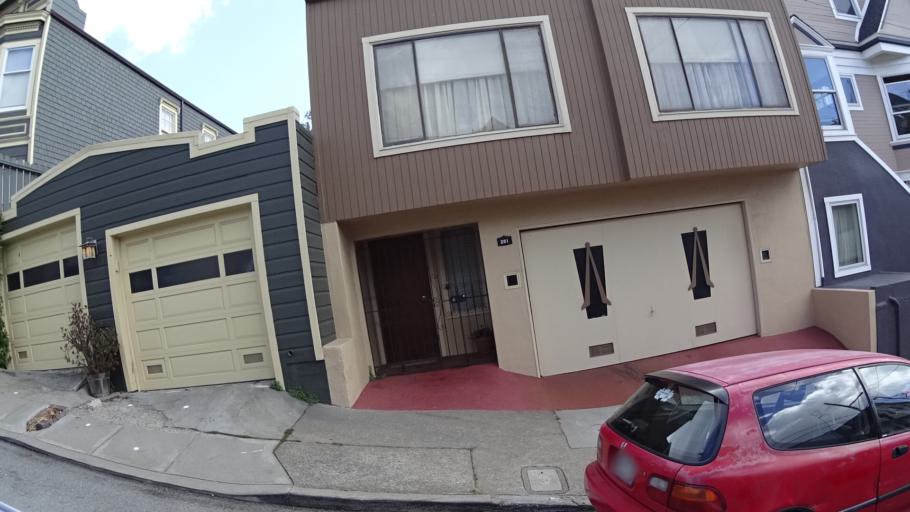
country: US
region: California
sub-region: San Francisco County
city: San Francisco
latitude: 37.7407
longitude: -122.4158
